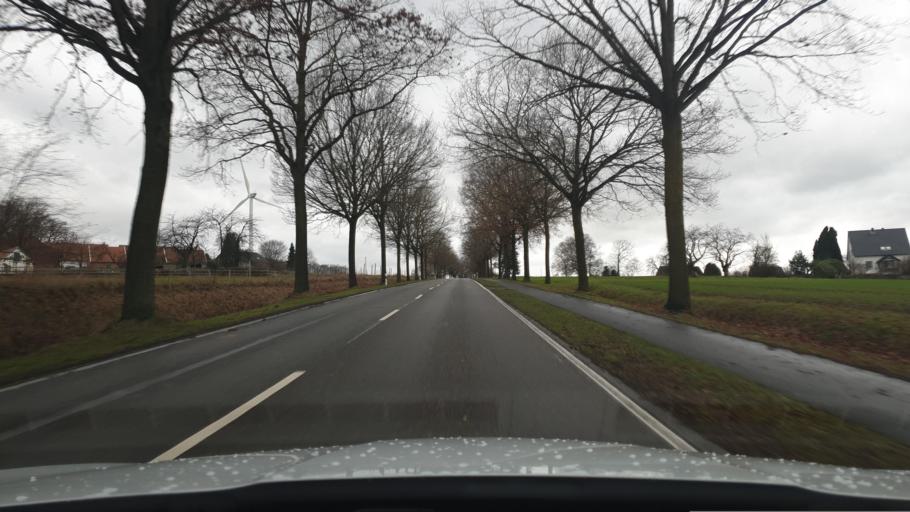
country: DE
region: North Rhine-Westphalia
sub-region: Regierungsbezirk Detmold
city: Vlotho
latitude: 52.1352
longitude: 8.8143
